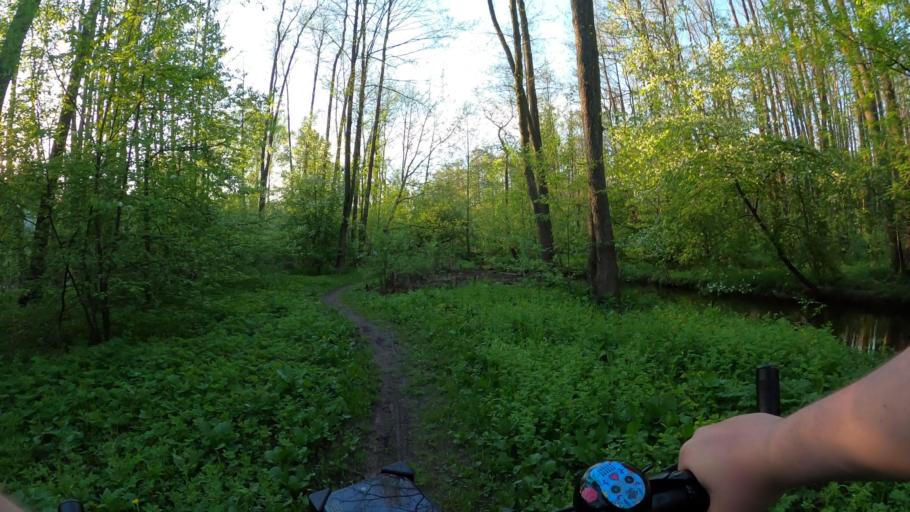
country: RU
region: Moskovskaya
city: Kratovo
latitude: 55.5801
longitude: 38.1712
